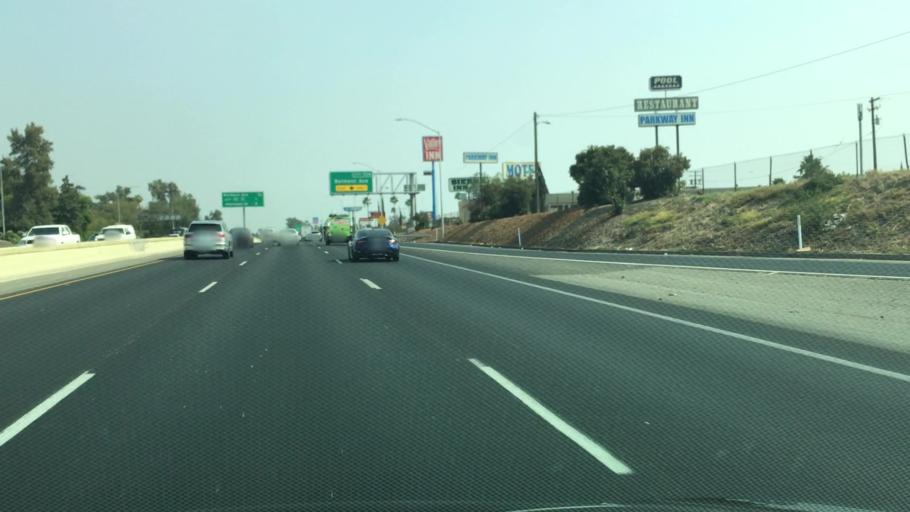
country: US
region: California
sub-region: Fresno County
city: West Park
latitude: 36.7560
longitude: -119.8290
